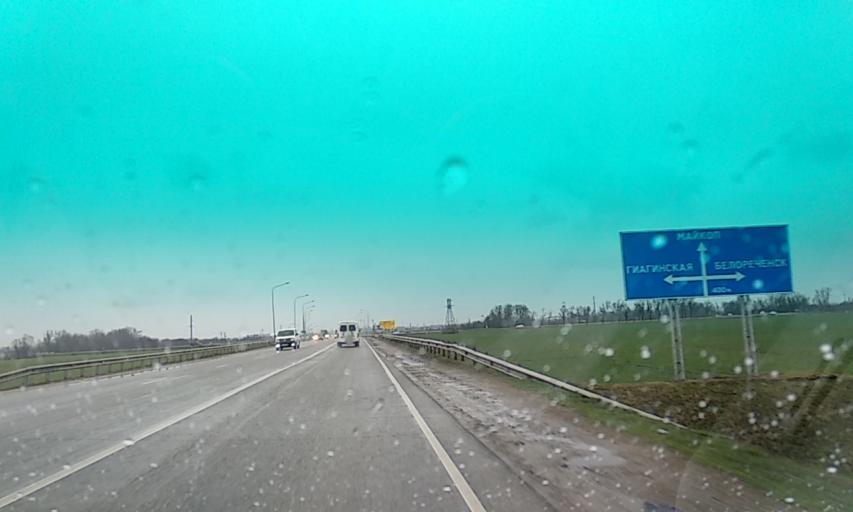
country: RU
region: Krasnodarskiy
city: Belorechensk
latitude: 44.8167
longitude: 39.8526
